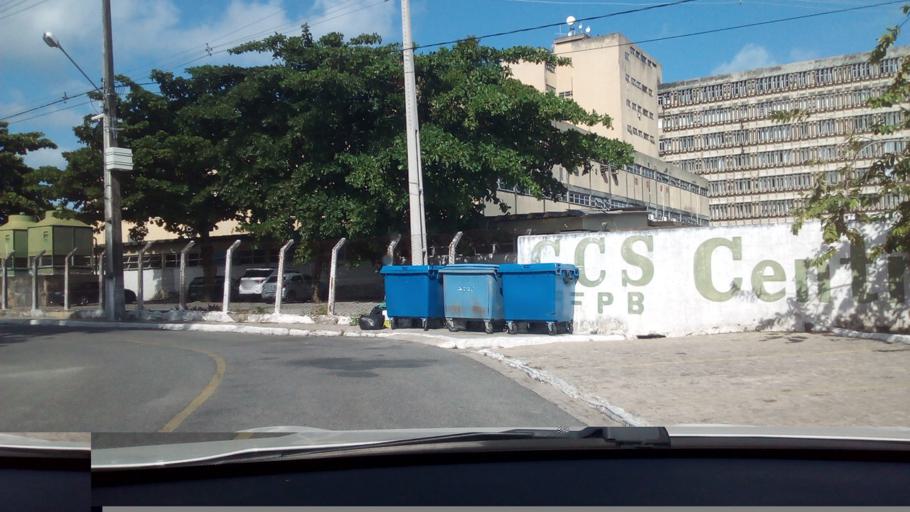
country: BR
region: Paraiba
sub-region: Joao Pessoa
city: Joao Pessoa
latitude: -7.1362
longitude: -34.8412
